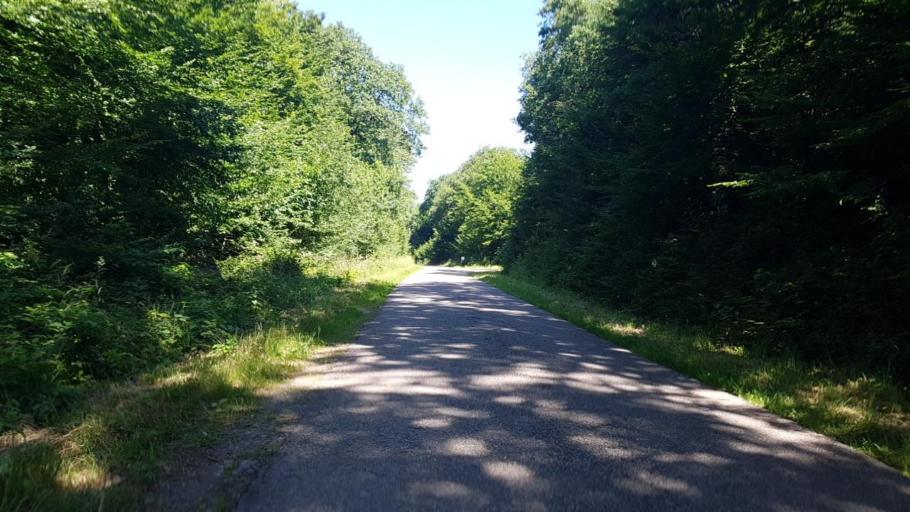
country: BE
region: Wallonia
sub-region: Province du Hainaut
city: Momignies
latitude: 50.0892
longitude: 4.2291
